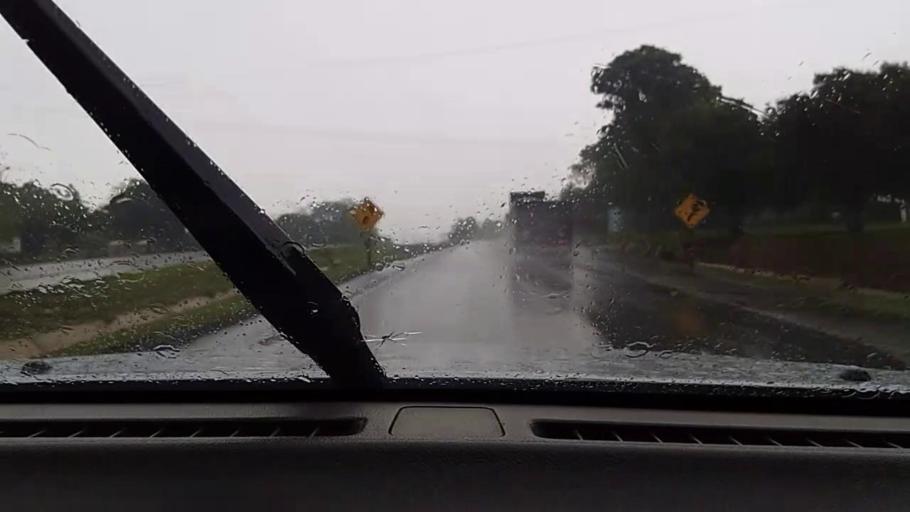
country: PY
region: Caaguazu
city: Repatriacion
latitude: -25.4460
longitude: -55.8856
